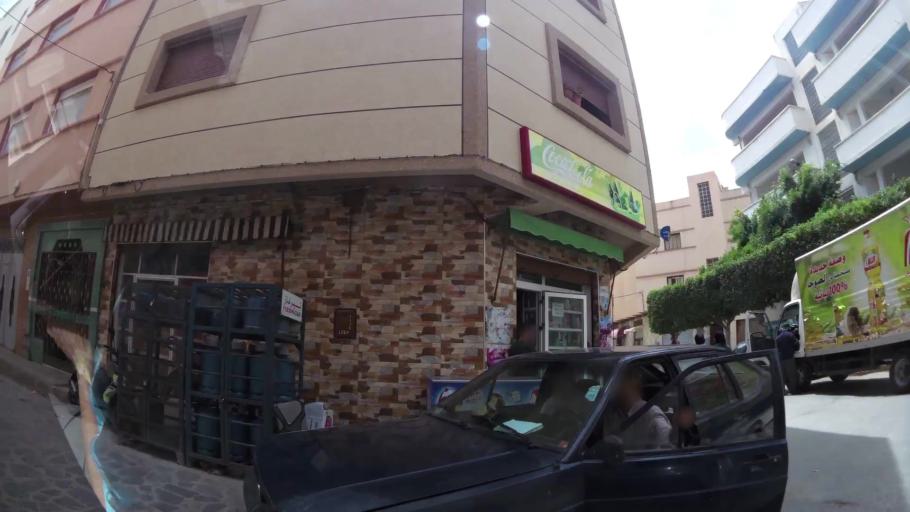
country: MA
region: Oriental
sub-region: Nador
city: Nador
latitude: 35.1732
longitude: -2.9222
